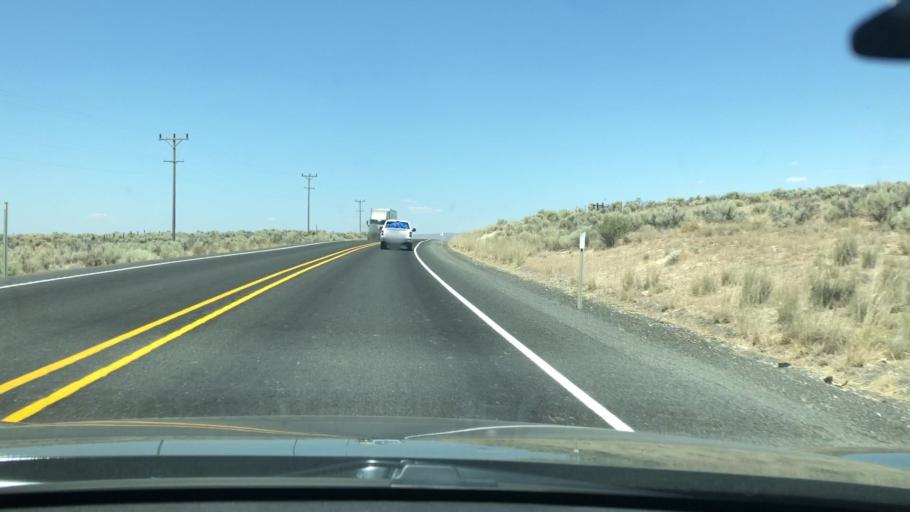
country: US
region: Idaho
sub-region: Owyhee County
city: Murphy
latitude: 42.9960
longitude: -117.0613
